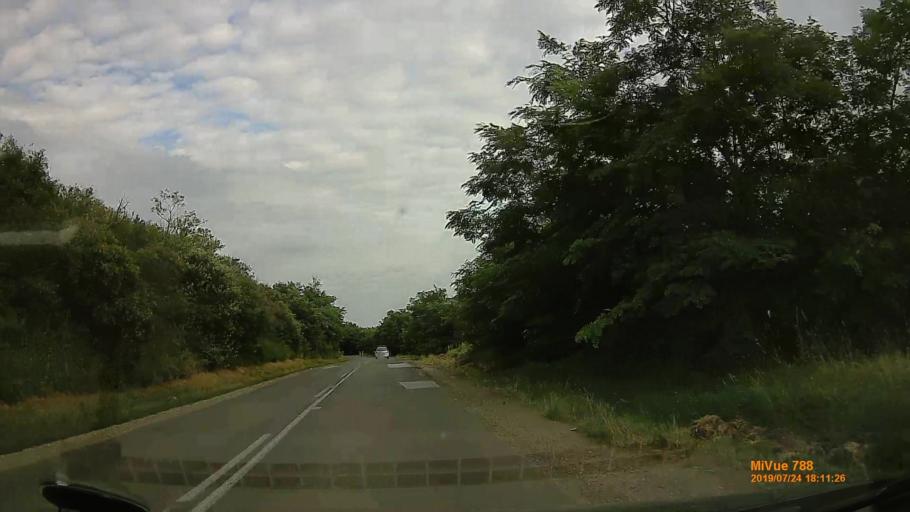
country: HU
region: Borsod-Abauj-Zemplen
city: Tallya
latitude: 48.2466
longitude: 21.1992
